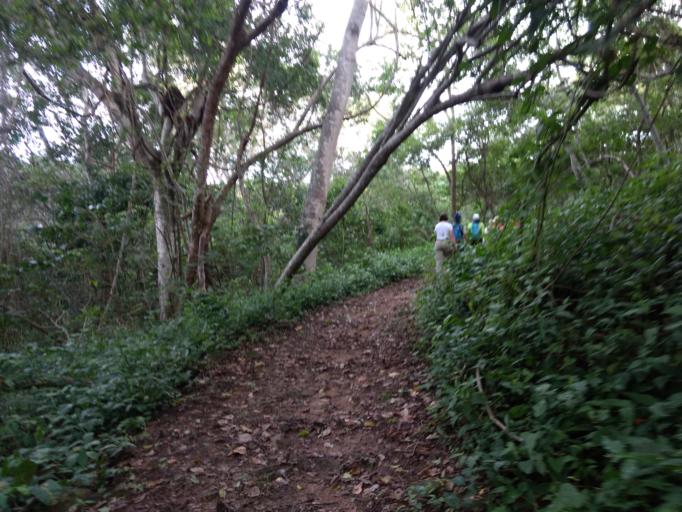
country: BR
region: Ceara
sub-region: Crateus
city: Crateus
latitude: -5.1415
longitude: -40.9179
